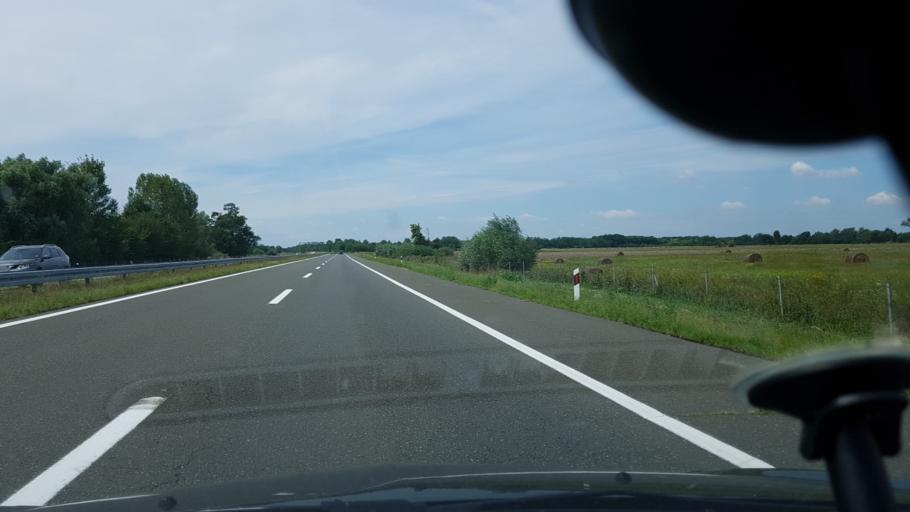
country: HR
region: Medimurska
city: Hodosan
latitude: 46.4131
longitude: 16.6310
